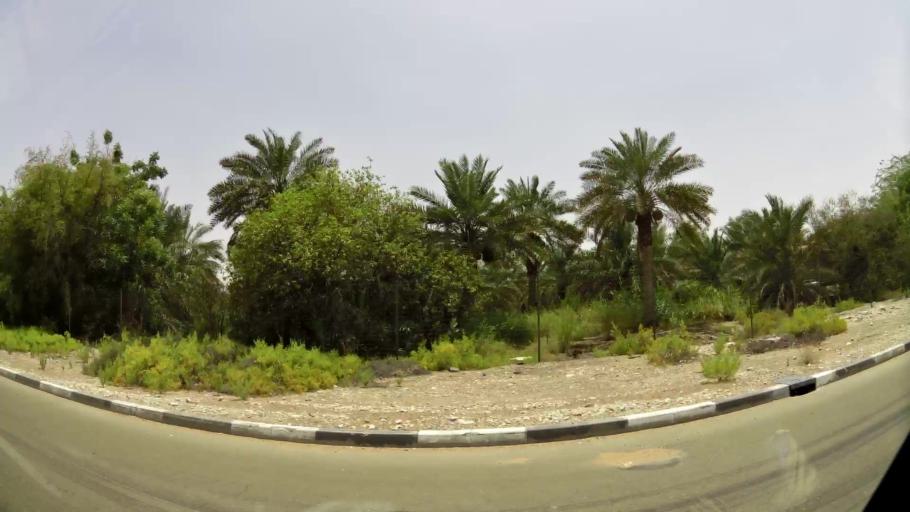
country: AE
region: Abu Dhabi
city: Al Ain
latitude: 24.2032
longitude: 55.7027
